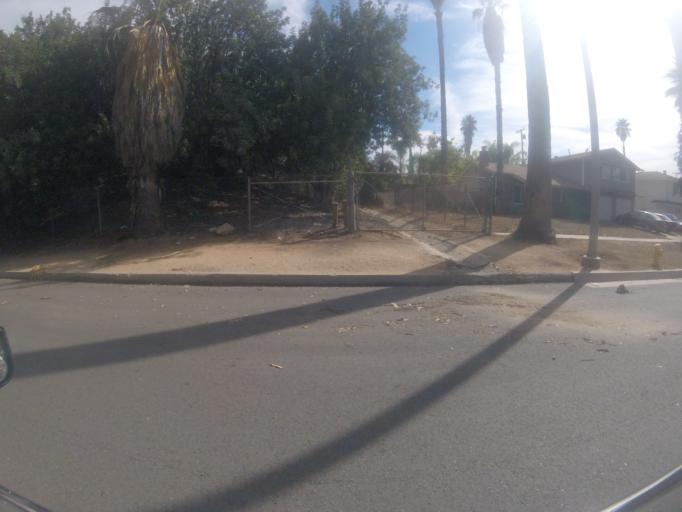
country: US
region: California
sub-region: San Bernardino County
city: Redlands
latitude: 34.0514
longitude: -117.1613
